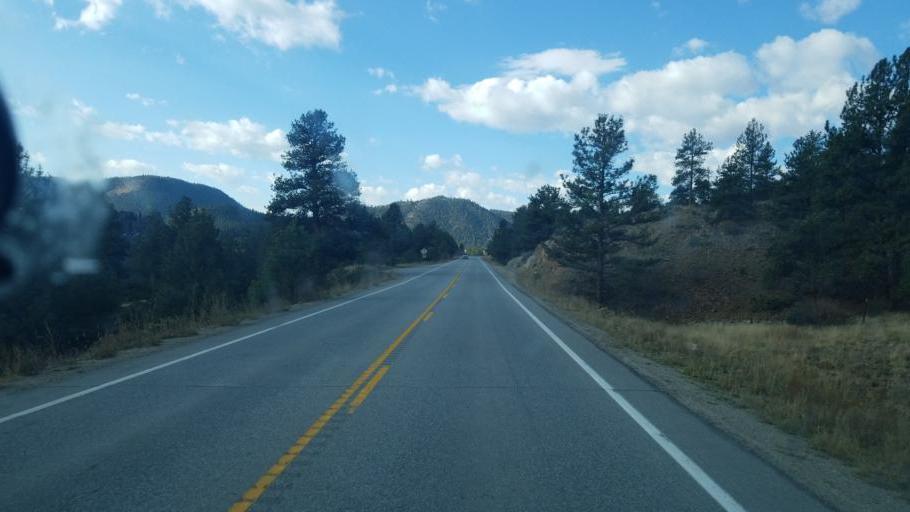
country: US
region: Colorado
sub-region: Chaffee County
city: Buena Vista
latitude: 38.8494
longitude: -105.9855
